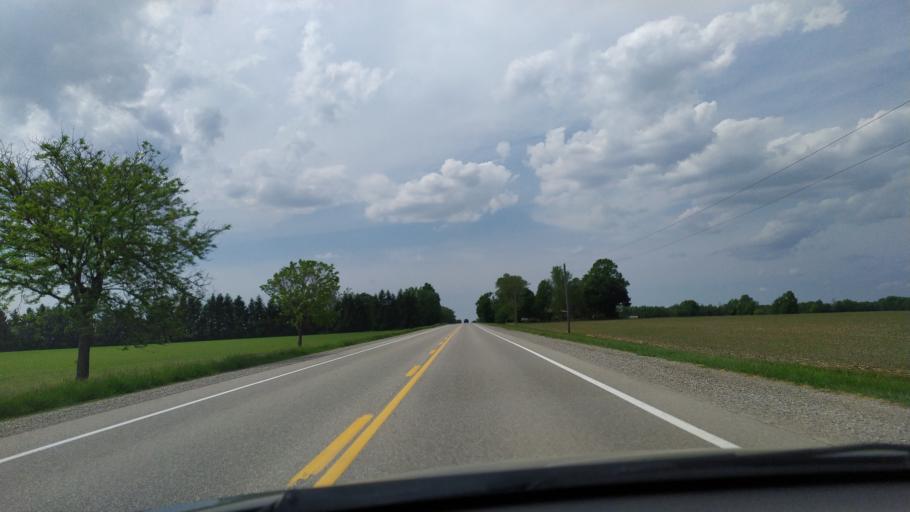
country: CA
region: Ontario
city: Dorchester
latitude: 43.1528
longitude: -81.0372
